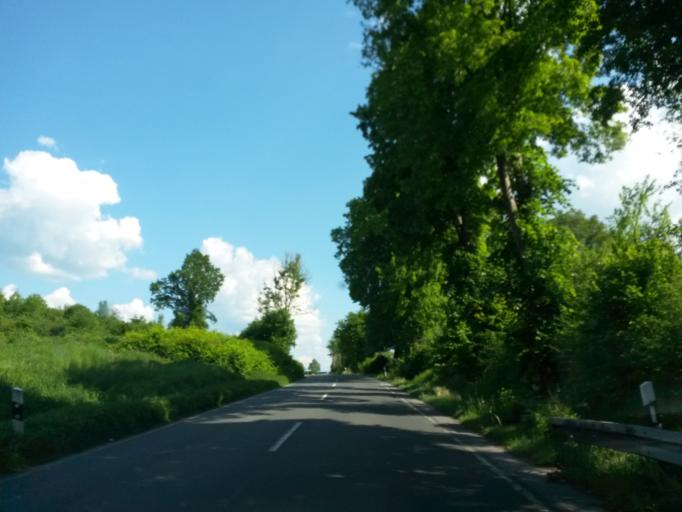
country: DE
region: North Rhine-Westphalia
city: Balve
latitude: 51.3168
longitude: 7.8711
